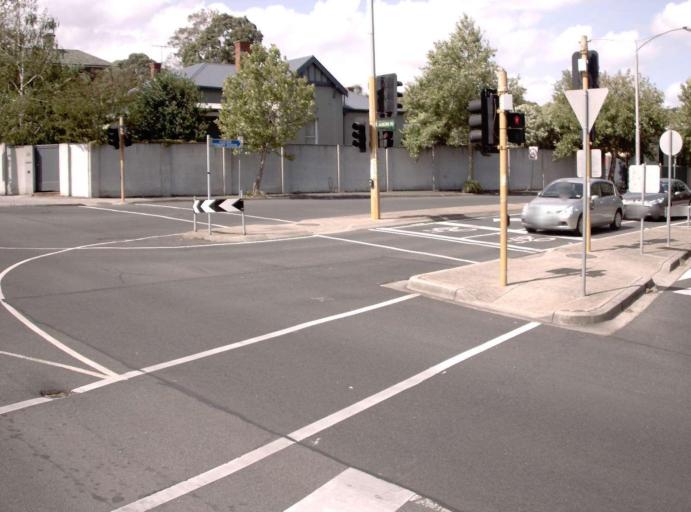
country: AU
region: Victoria
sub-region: Boroondara
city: Hawthorn East
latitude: -37.8200
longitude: 145.0455
